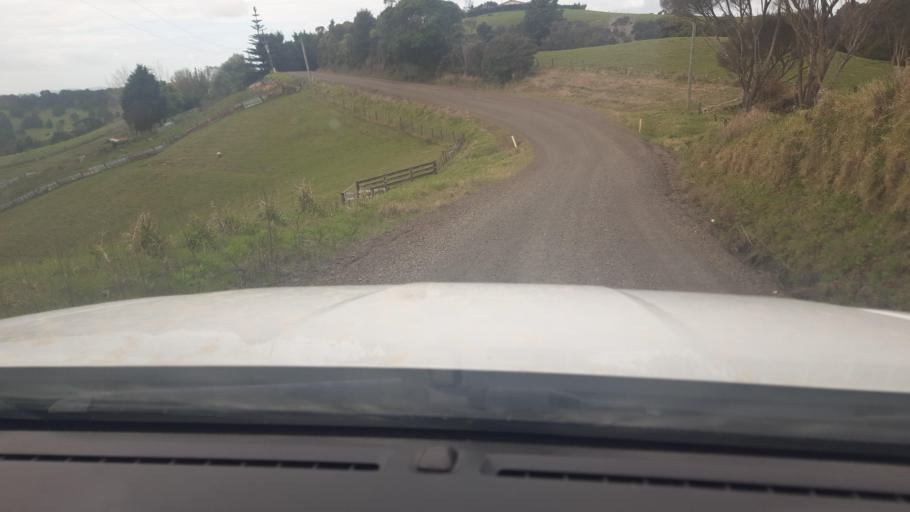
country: NZ
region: Northland
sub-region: Far North District
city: Kaitaia
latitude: -35.0747
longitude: 173.3234
